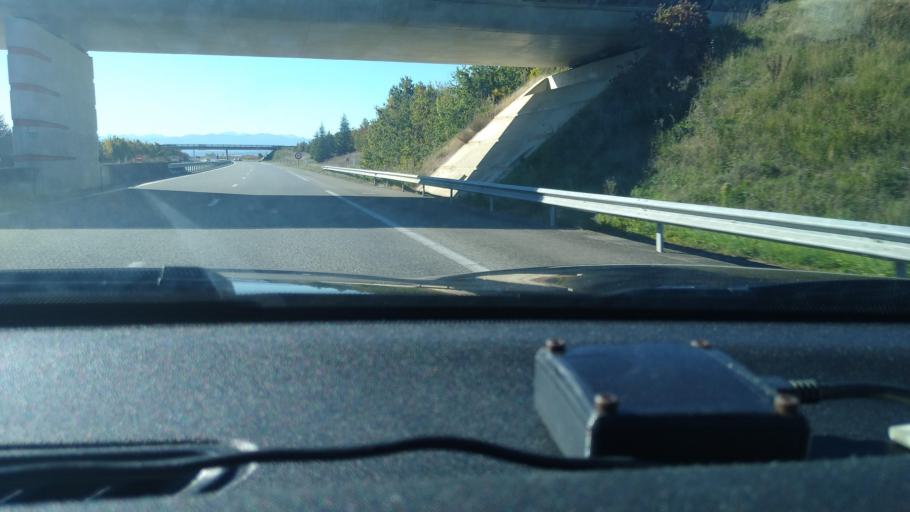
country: FR
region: Midi-Pyrenees
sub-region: Departement de l'Ariege
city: Mazeres
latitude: 43.2360
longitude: 1.6415
